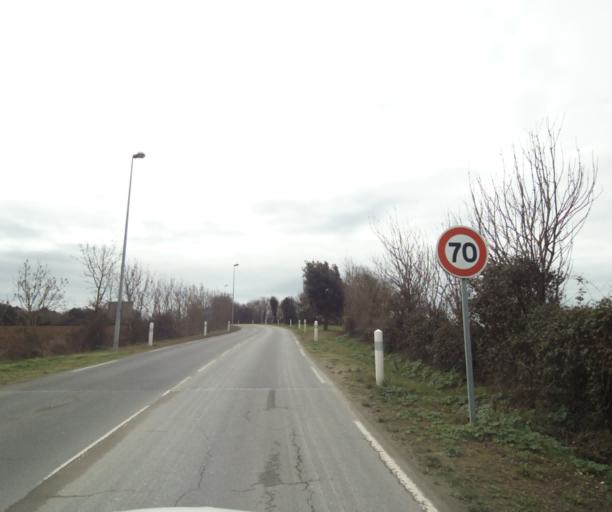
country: FR
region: Poitou-Charentes
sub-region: Departement de la Charente-Maritime
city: Nieul-sur-Mer
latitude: 46.1885
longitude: -1.1813
